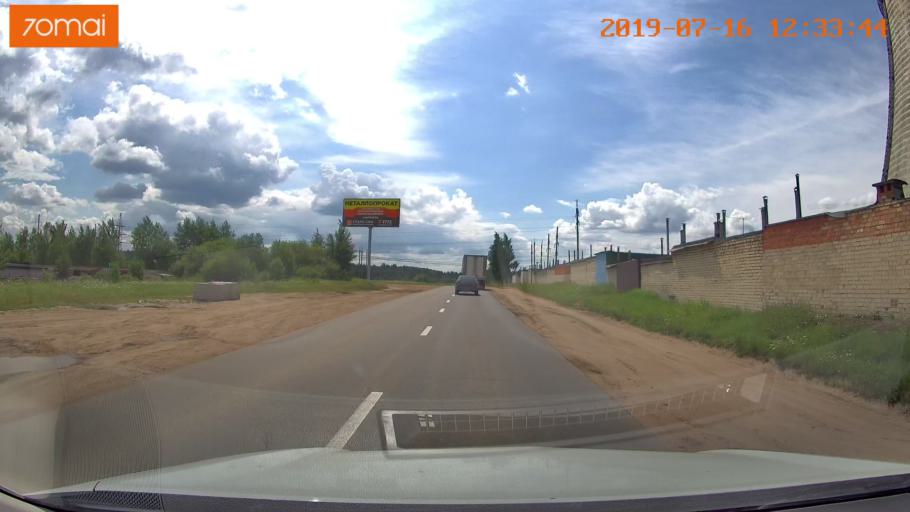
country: BY
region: Minsk
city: Malinovka
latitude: 53.8710
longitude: 27.4102
